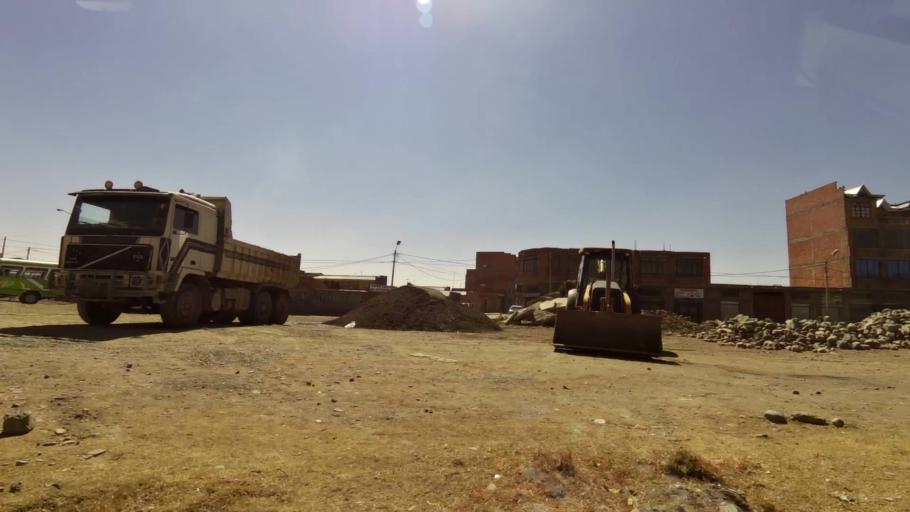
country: BO
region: La Paz
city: La Paz
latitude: -16.5503
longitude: -68.1895
